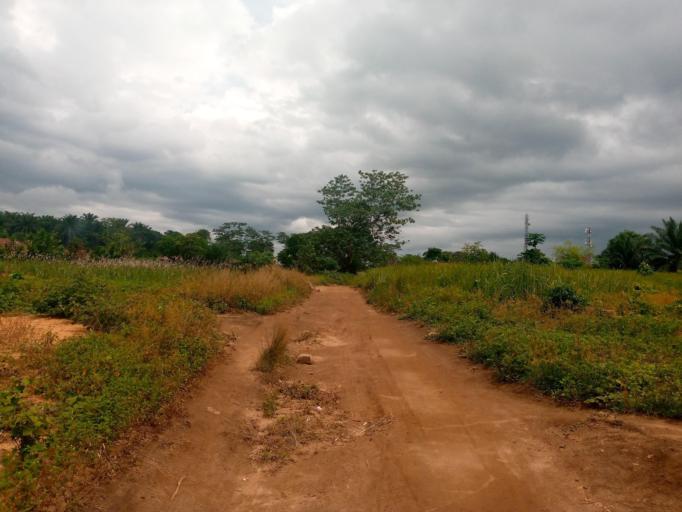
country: SL
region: Southern Province
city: Mogbwemo
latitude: 7.6002
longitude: -12.1702
